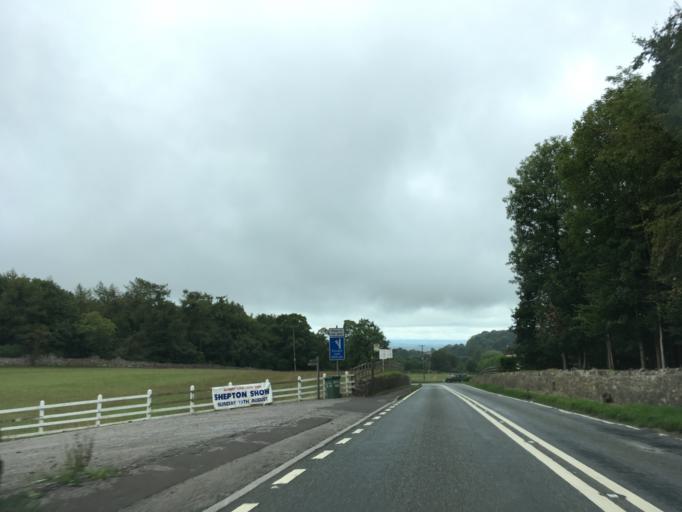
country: GB
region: England
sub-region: Somerset
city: Mendip
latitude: 51.2215
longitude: -2.6354
